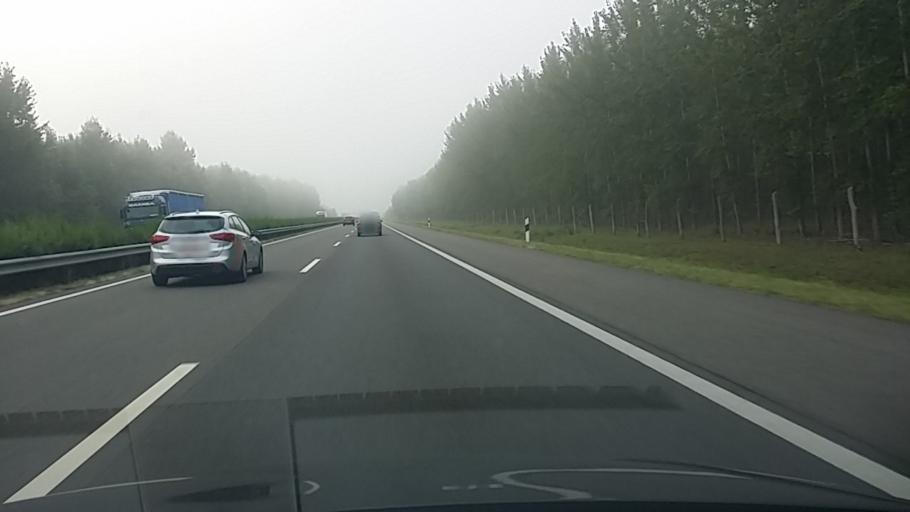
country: HU
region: Csongrad
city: Csengele
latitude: 46.5192
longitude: 19.9007
